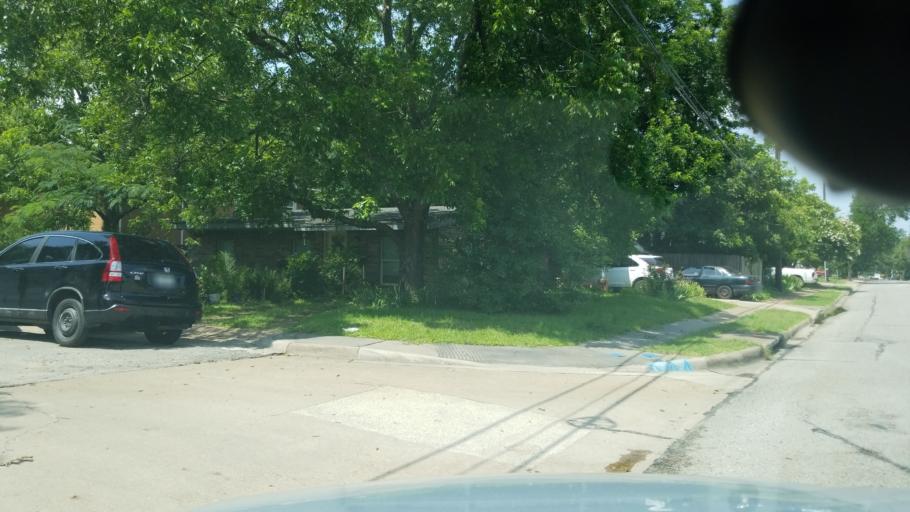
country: US
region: Texas
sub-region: Dallas County
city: Irving
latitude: 32.8333
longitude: -96.9472
